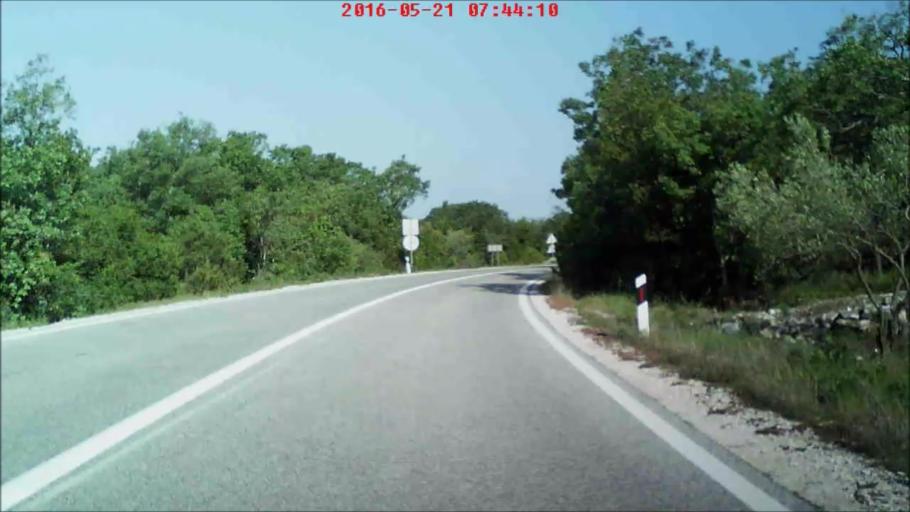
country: HR
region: Dubrovacko-Neretvanska
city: Podgora
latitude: 42.8145
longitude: 17.7818
